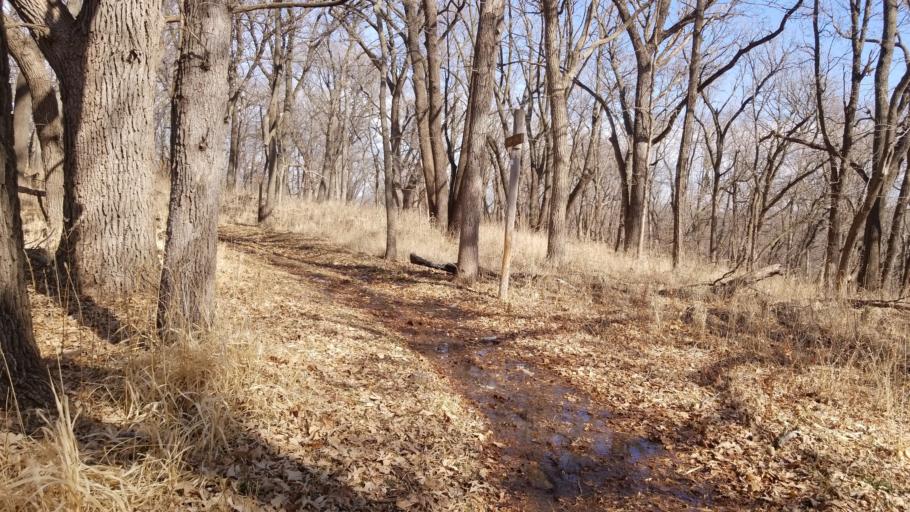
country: US
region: Nebraska
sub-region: Sarpy County
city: Bellevue
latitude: 41.1705
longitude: -95.9017
